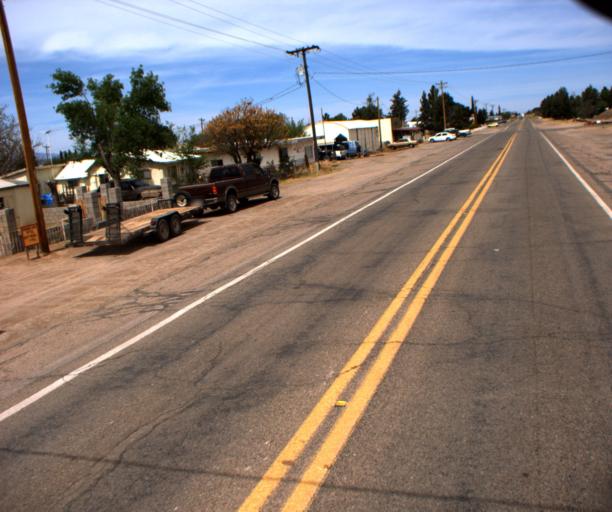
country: US
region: Arizona
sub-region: Cochise County
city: Bisbee
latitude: 31.6842
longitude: -109.6874
